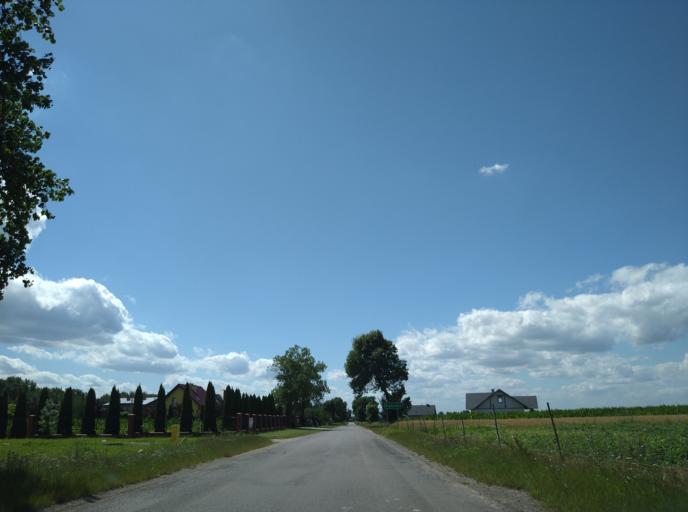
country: PL
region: Masovian Voivodeship
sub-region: Powiat grojecki
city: Goszczyn
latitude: 51.6683
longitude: 20.8767
